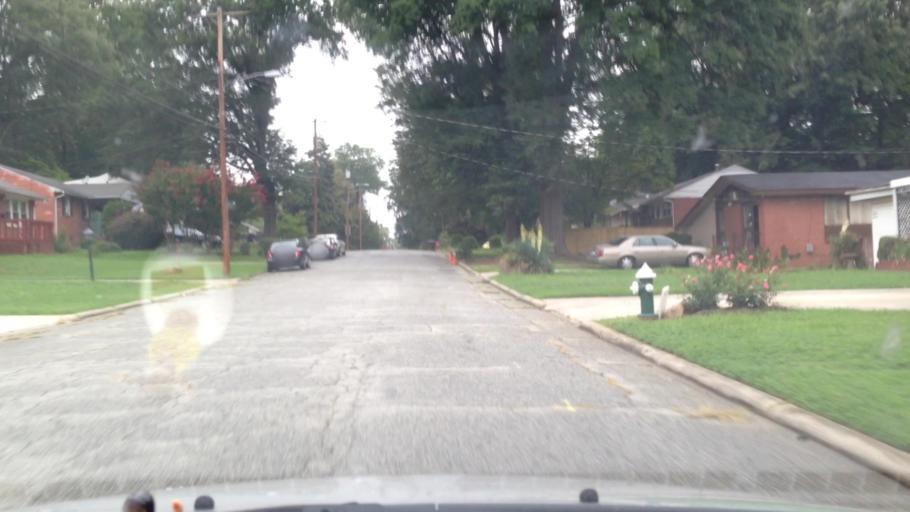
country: US
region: North Carolina
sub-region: Guilford County
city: Greensboro
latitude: 36.0525
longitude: -79.7635
